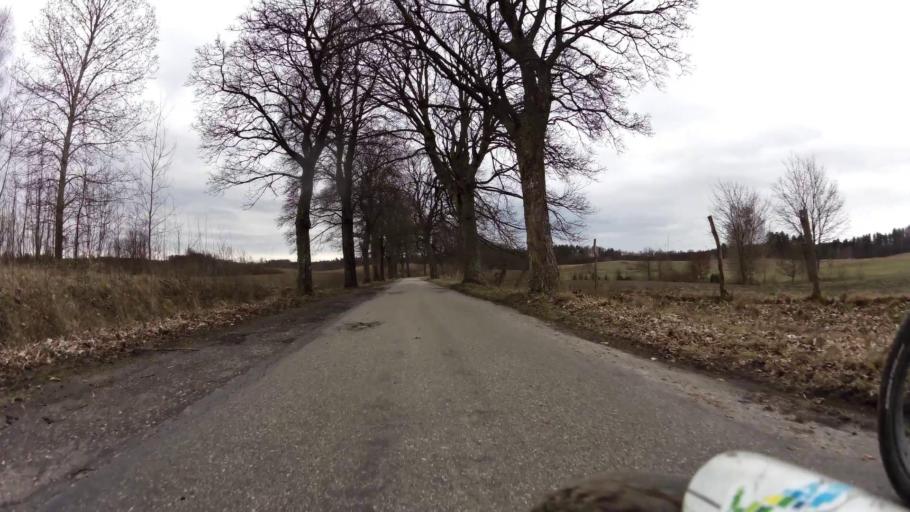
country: PL
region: Pomeranian Voivodeship
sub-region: Powiat bytowski
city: Trzebielino
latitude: 54.1023
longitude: 17.1304
